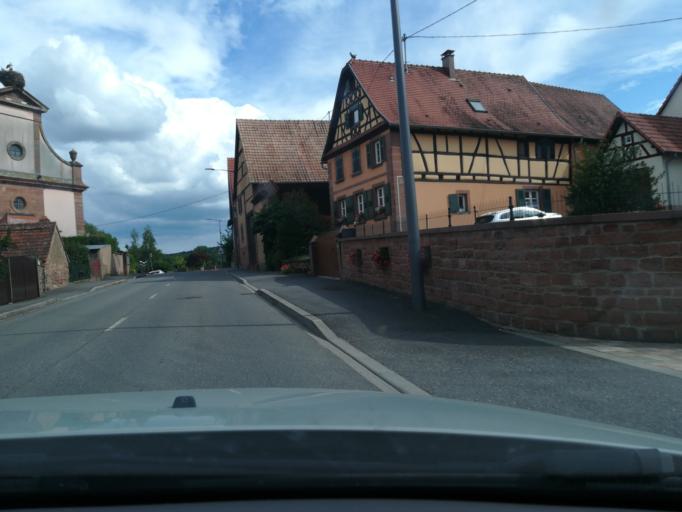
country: FR
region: Alsace
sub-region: Departement du Bas-Rhin
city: Ingwiller
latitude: 48.8591
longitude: 7.4963
